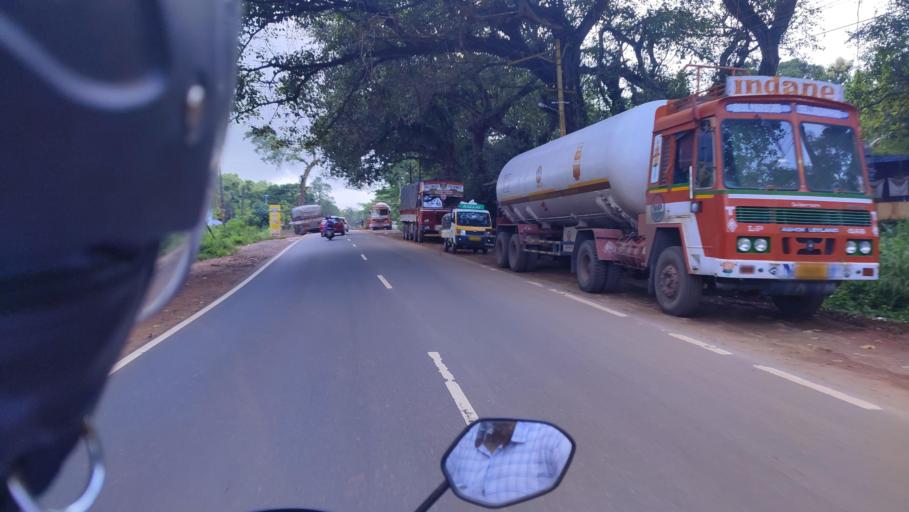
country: IN
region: Kerala
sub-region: Kasaragod District
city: Nileshwar
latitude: 12.2275
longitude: 75.1566
